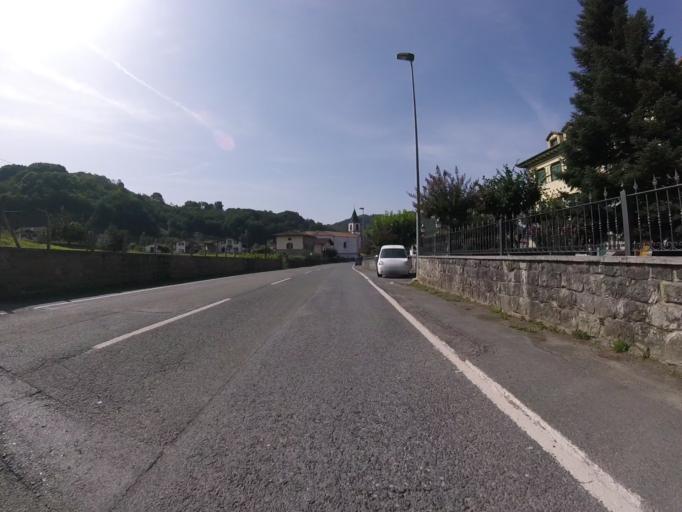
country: ES
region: Navarre
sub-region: Provincia de Navarra
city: Doneztebe
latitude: 43.1416
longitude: -1.6048
